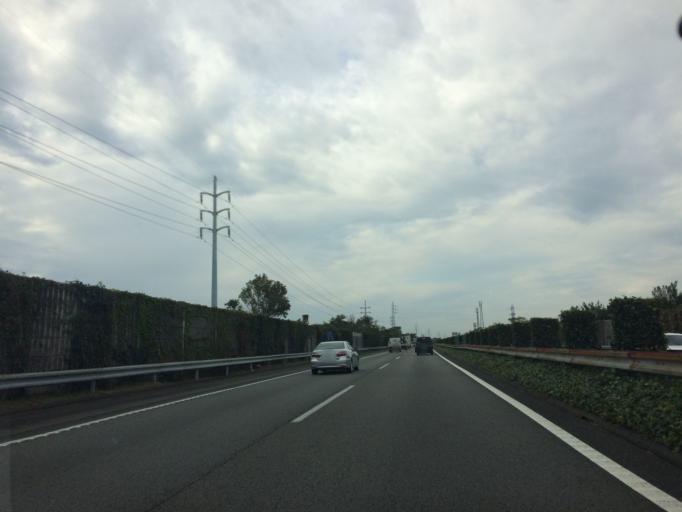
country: JP
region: Shizuoka
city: Fujieda
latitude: 34.8328
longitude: 138.2778
